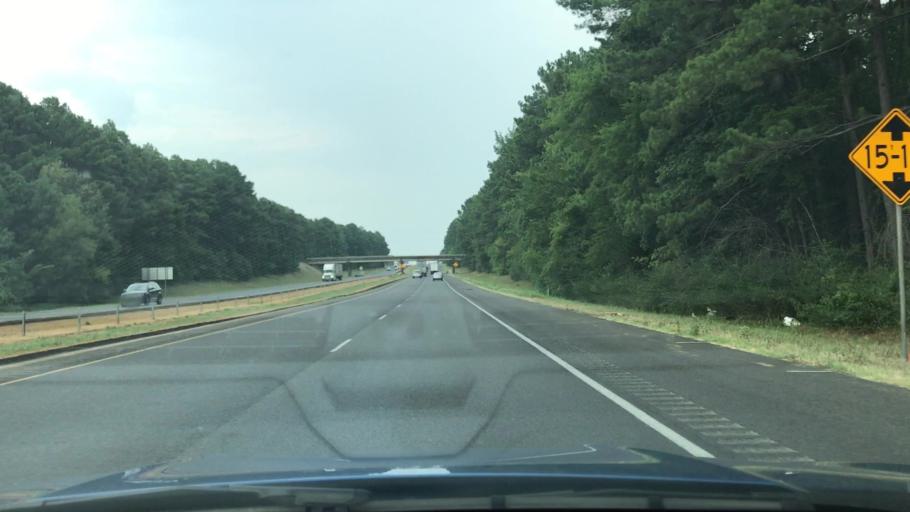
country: US
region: Texas
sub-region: Harrison County
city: Marshall
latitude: 32.4944
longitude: -94.2760
